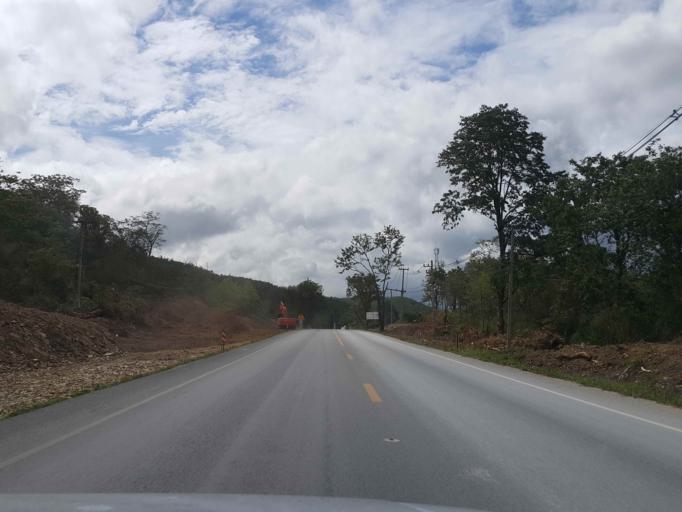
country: TH
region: Tak
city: Tak
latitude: 16.8001
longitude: 99.0040
